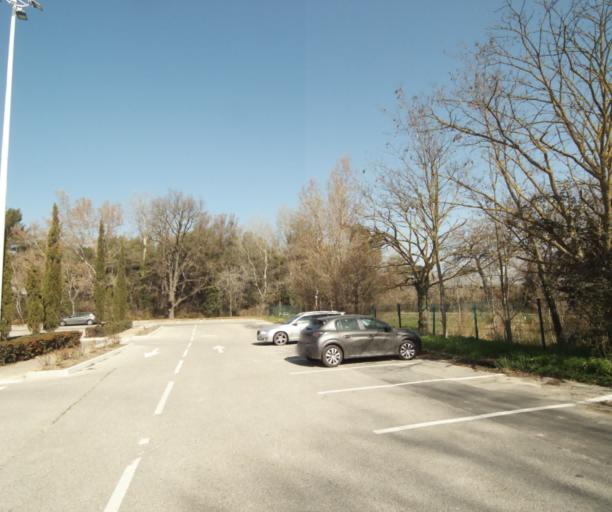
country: FR
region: Provence-Alpes-Cote d'Azur
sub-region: Departement des Bouches-du-Rhone
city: Cabries
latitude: 43.4331
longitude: 5.3976
